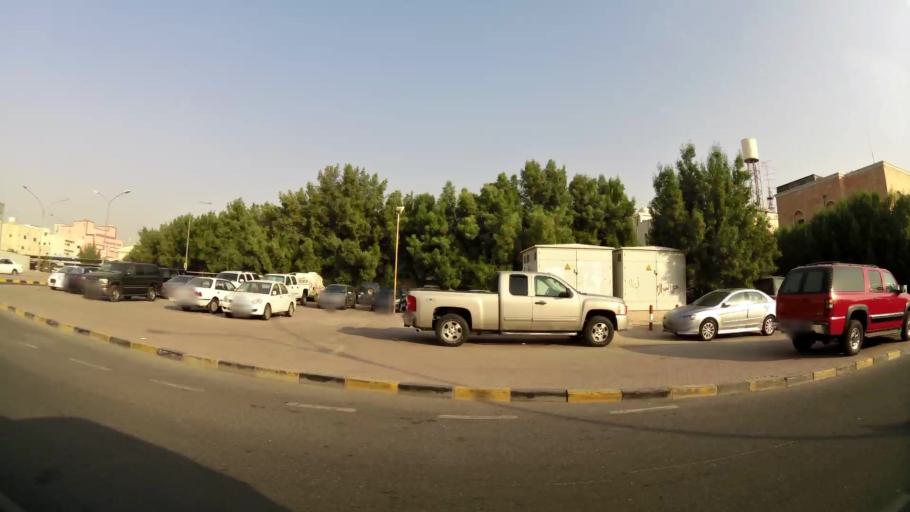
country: KW
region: Muhafazat Hawalli
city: Salwa
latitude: 29.3023
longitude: 48.0719
